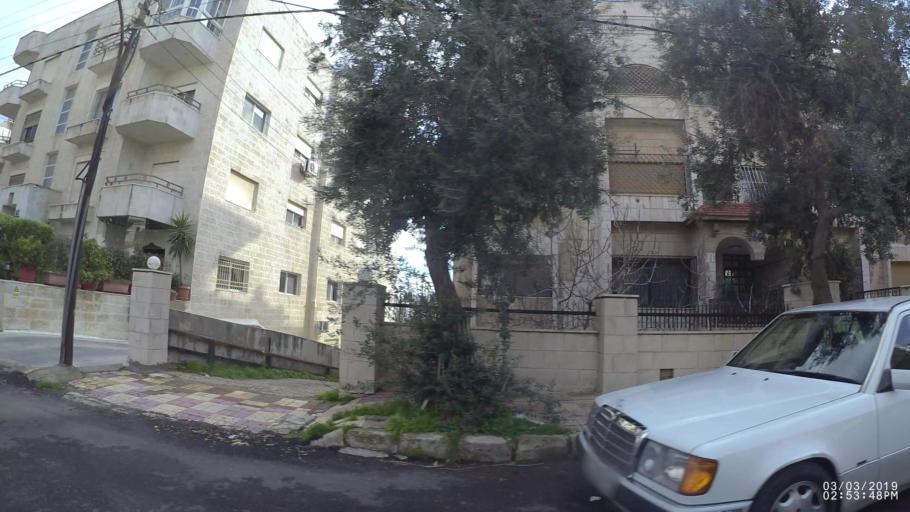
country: JO
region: Amman
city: Amman
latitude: 31.9624
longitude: 35.8955
